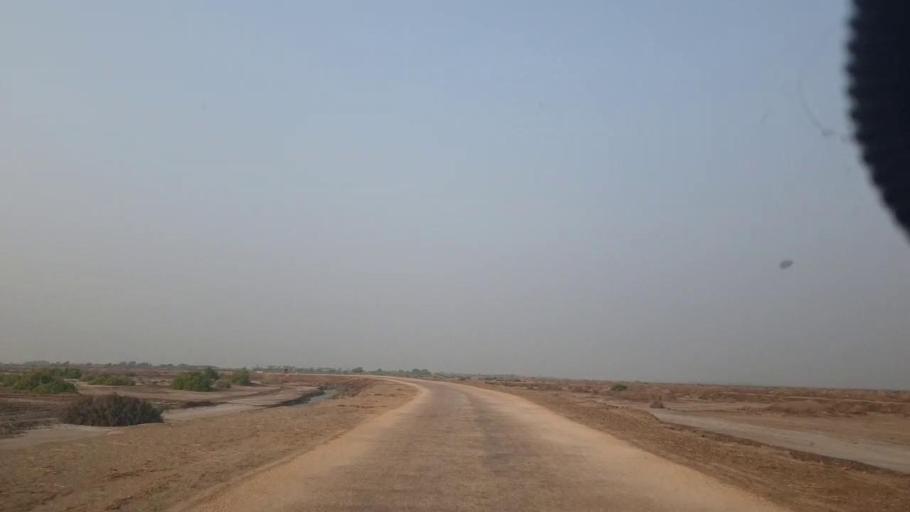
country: PK
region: Sindh
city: Bulri
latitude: 24.8506
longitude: 68.4048
